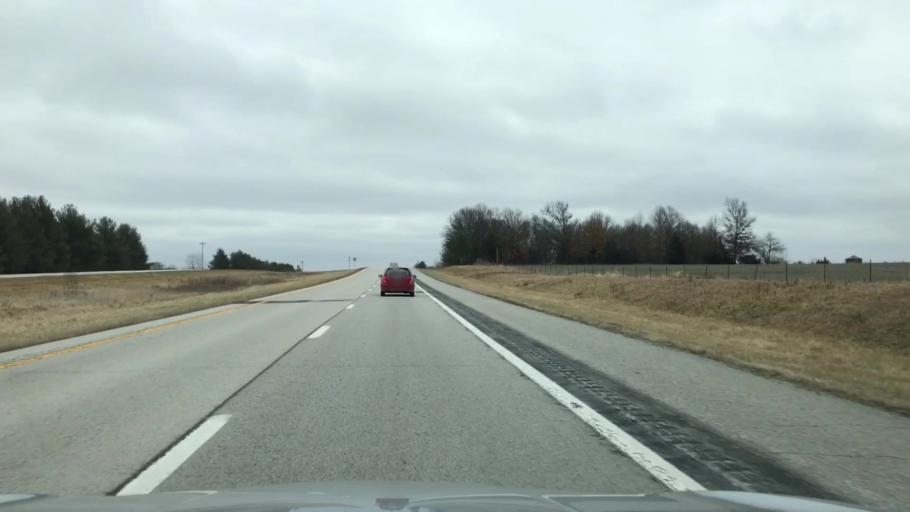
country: US
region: Missouri
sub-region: Livingston County
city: Chillicothe
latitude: 39.7771
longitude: -93.3714
